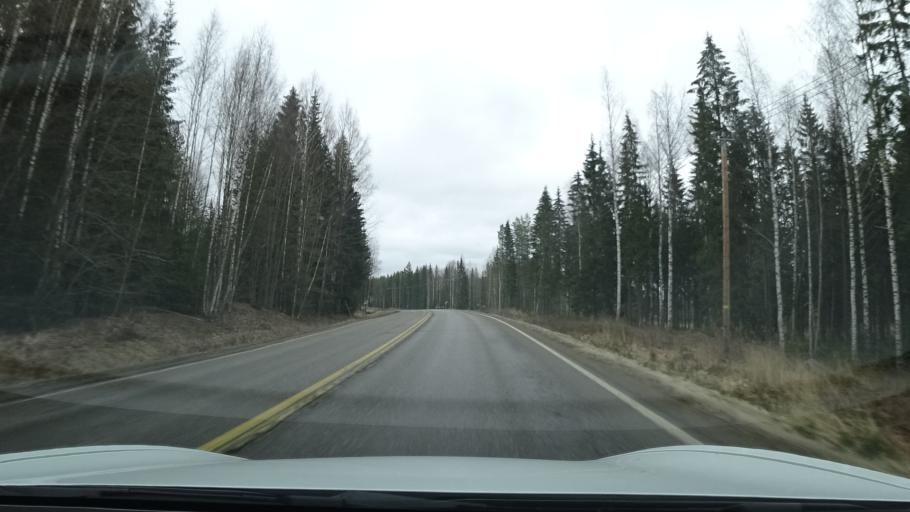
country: FI
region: Uusimaa
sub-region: Porvoo
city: Pukkila
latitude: 60.6457
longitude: 25.6523
